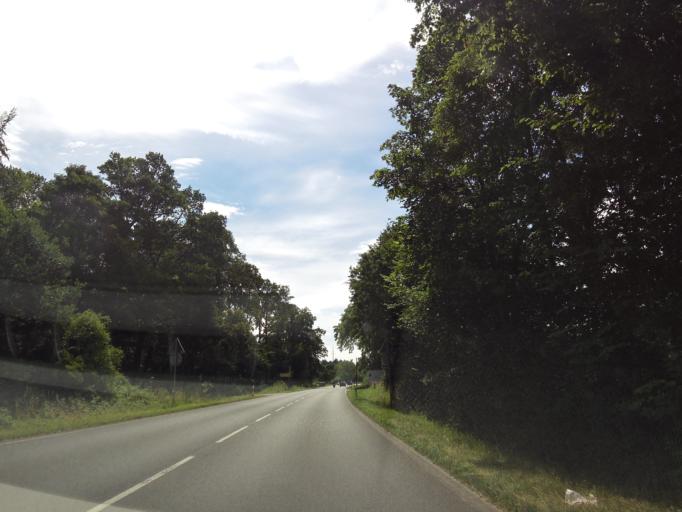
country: DE
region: Lower Saxony
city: Furstenberg
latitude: 51.7130
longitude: 9.3743
